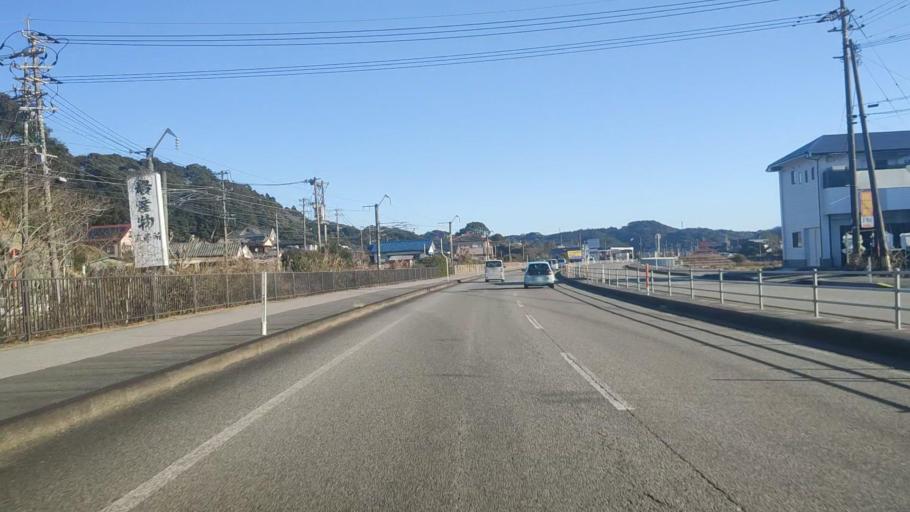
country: JP
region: Miyazaki
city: Nobeoka
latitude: 32.4816
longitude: 131.6575
